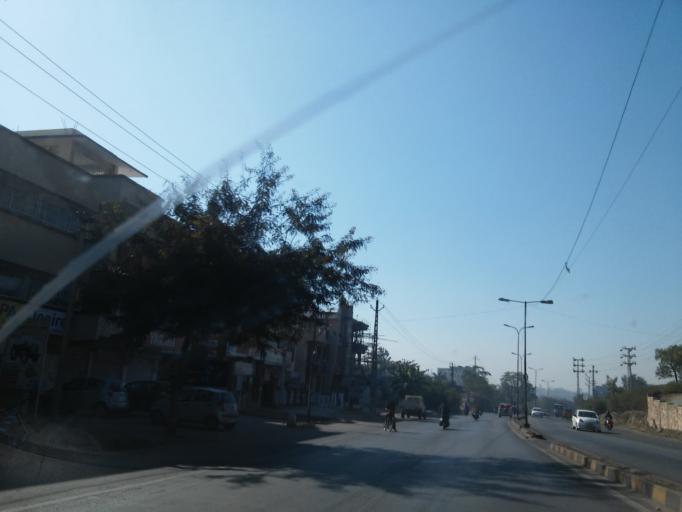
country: IN
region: Rajasthan
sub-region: Udaipur
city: Udaipur
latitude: 24.5568
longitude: 73.6924
